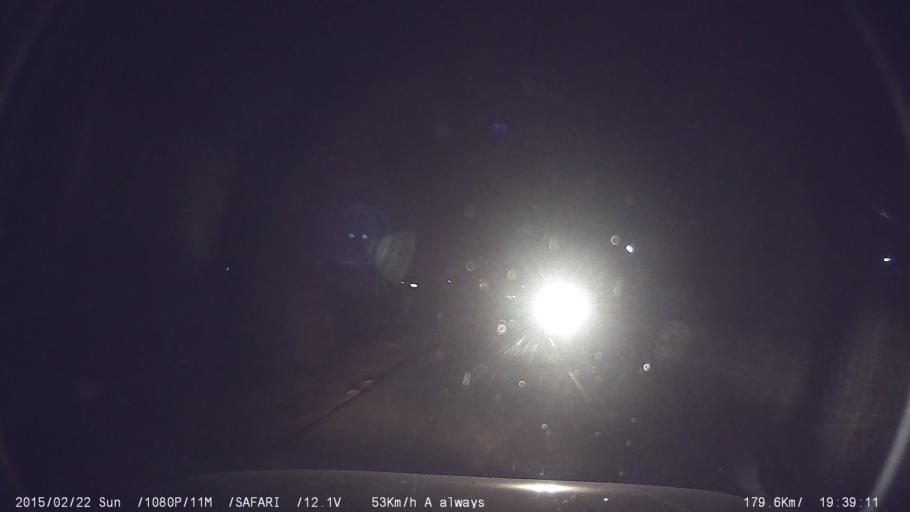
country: IN
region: Tamil Nadu
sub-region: Theni
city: Devadanappatti
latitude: 10.1453
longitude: 77.6357
